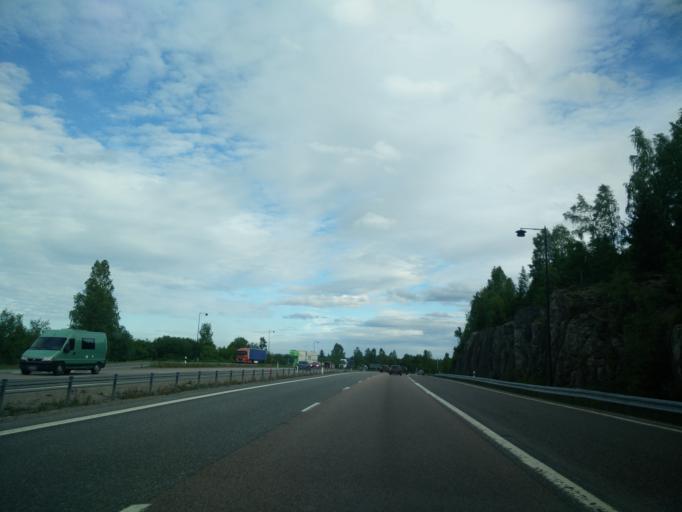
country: SE
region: Vaesternorrland
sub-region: Sundsvalls Kommun
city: Sundsbruk
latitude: 62.4589
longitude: 17.3423
